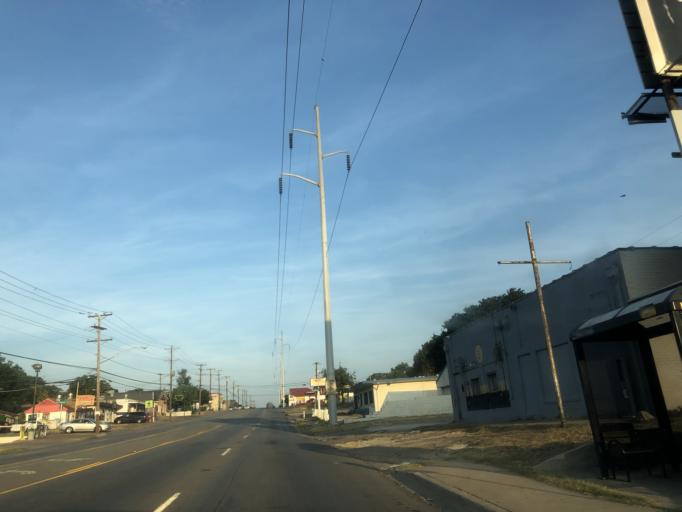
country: US
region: Texas
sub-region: Dallas County
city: Cockrell Hill
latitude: 32.7496
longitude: -96.8680
